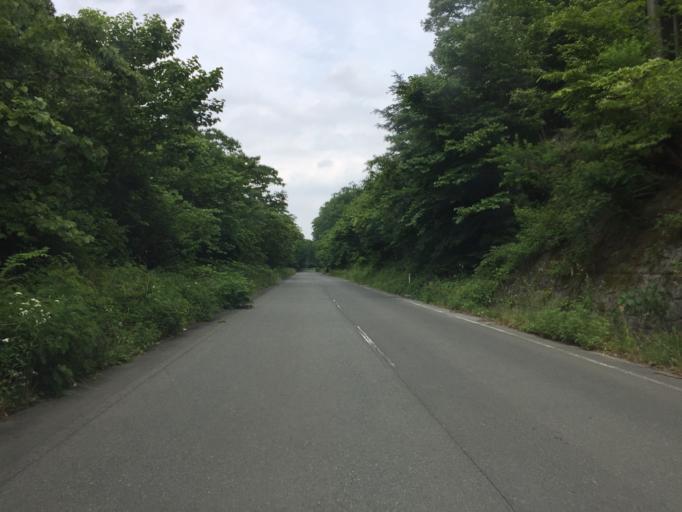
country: JP
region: Miyagi
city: Marumori
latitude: 37.8764
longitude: 140.8710
